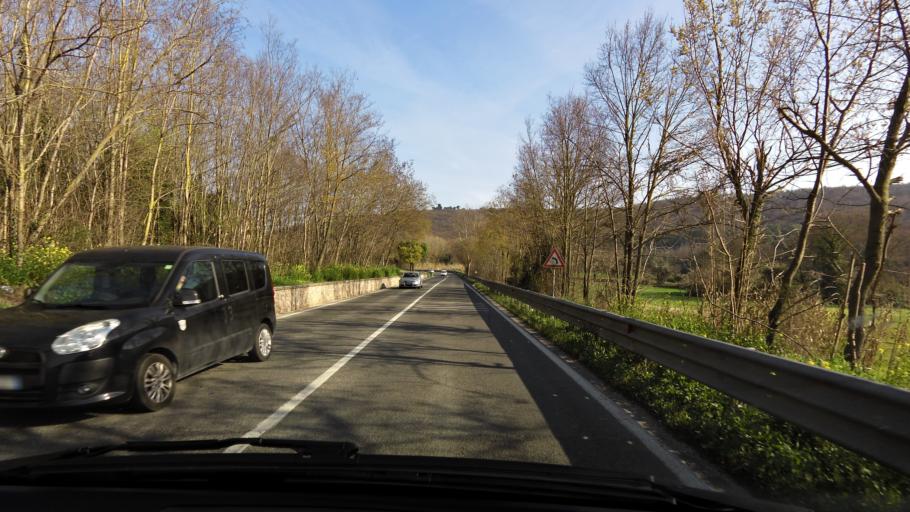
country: IT
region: The Marches
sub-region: Provincia di Ancona
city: Villa Musone
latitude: 43.4721
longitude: 13.5852
